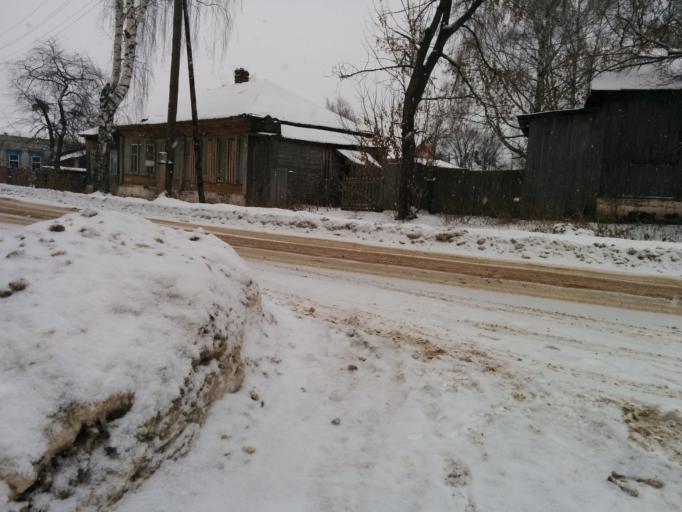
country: RU
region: Perm
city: Okhansk
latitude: 57.7269
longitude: 55.3866
